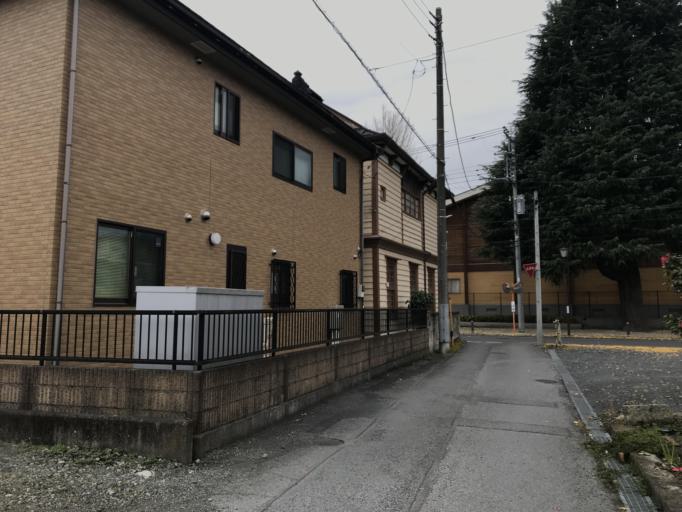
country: JP
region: Tochigi
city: Kanuma
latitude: 36.5649
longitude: 139.7457
